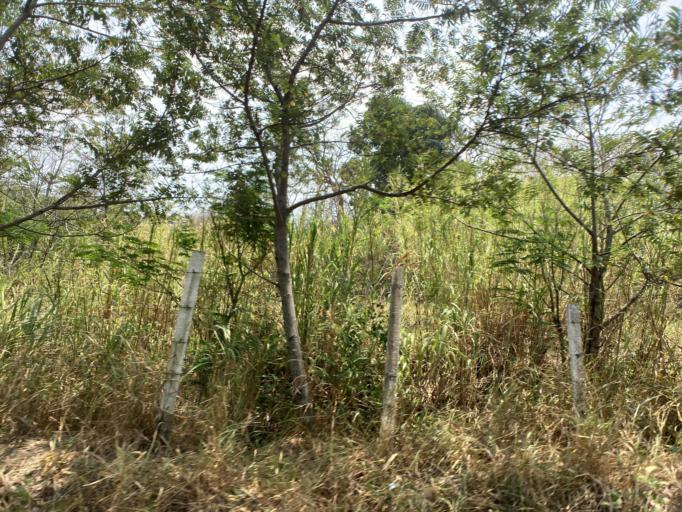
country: GT
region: Santa Rosa
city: Pueblo Nuevo Vinas
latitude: 14.3188
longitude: -90.5325
